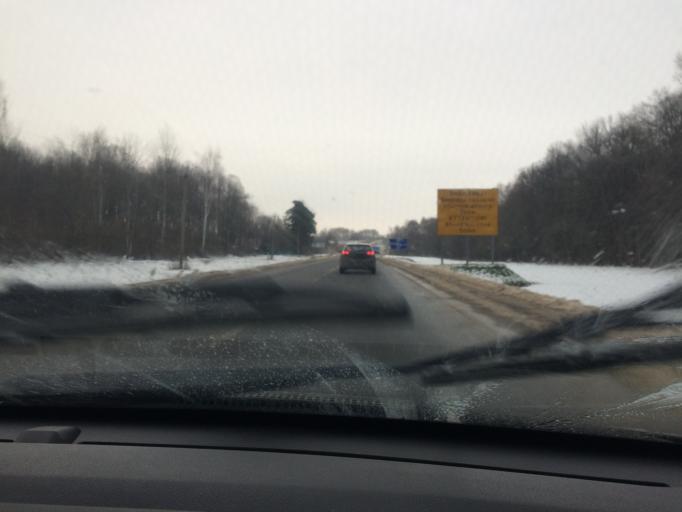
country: RU
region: Tula
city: Venev
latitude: 54.3369
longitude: 38.1390
